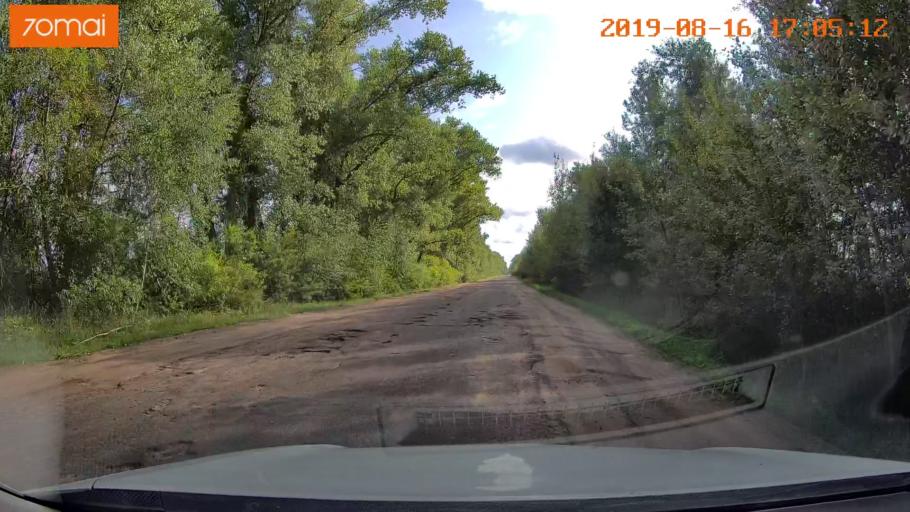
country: BY
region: Mogilev
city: Yalizava
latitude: 53.2389
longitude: 28.9457
